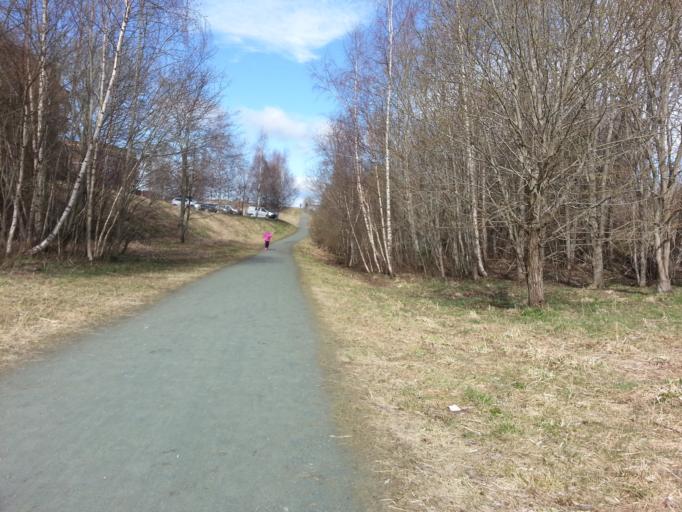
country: NO
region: Sor-Trondelag
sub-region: Trondheim
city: Trondheim
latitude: 63.4152
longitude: 10.4386
